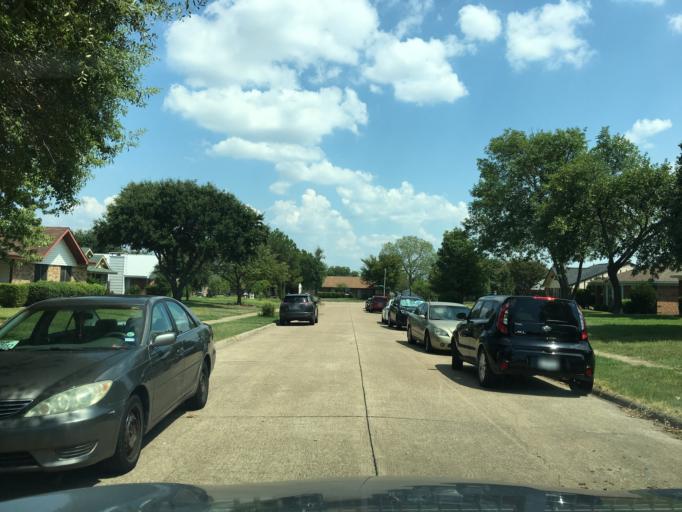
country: US
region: Texas
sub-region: Dallas County
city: Garland
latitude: 32.9462
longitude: -96.6636
